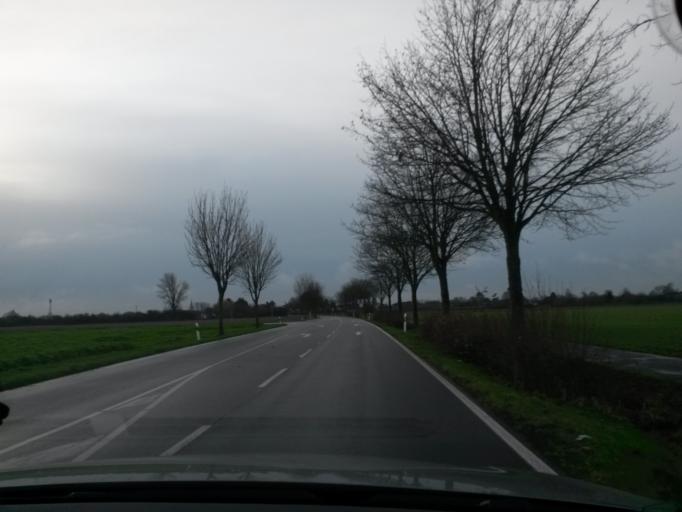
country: DE
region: North Rhine-Westphalia
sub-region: Regierungsbezirk Dusseldorf
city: Alpen
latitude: 51.6265
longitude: 6.5326
